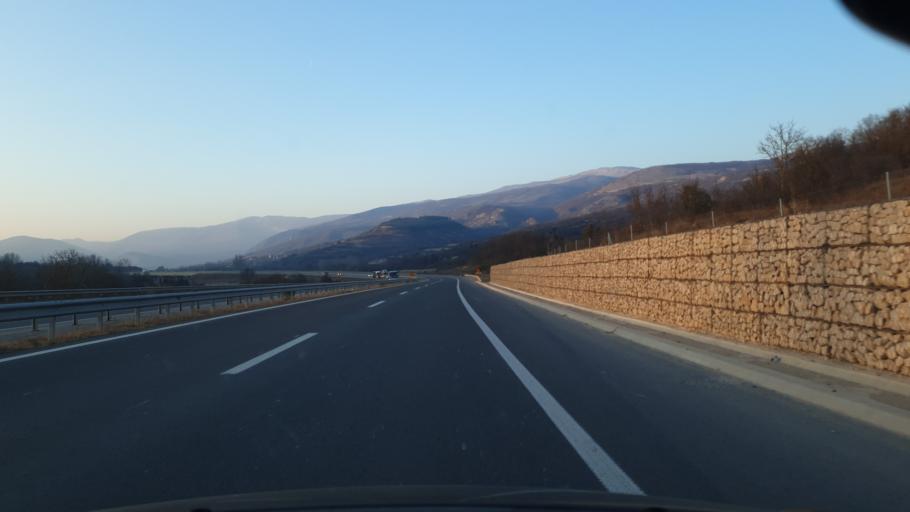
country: RS
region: Central Serbia
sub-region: Pirotski Okrug
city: Bela Palanka
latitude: 43.2523
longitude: 22.2698
